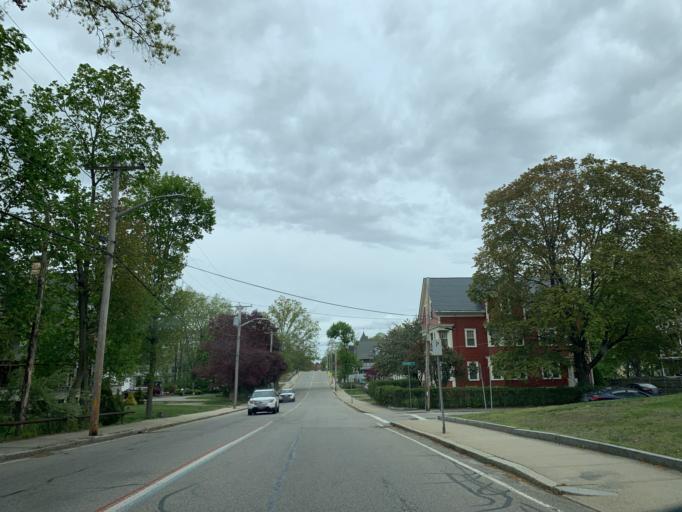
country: US
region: Massachusetts
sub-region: Bristol County
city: Attleboro
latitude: 41.9390
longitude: -71.2918
